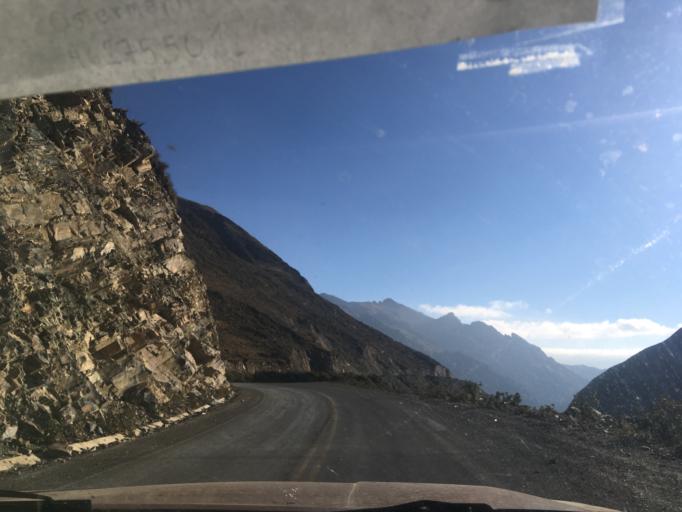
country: BO
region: La Paz
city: Quime
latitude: -17.0185
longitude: -67.2791
